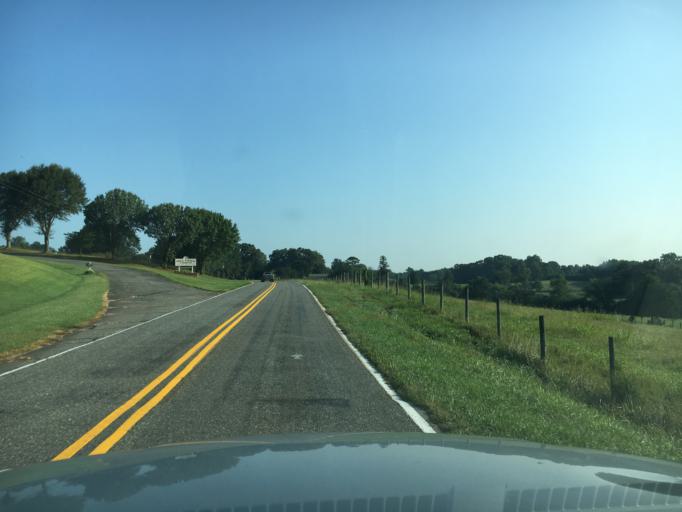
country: US
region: North Carolina
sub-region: Polk County
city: Columbus
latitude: 35.2409
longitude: -82.0537
